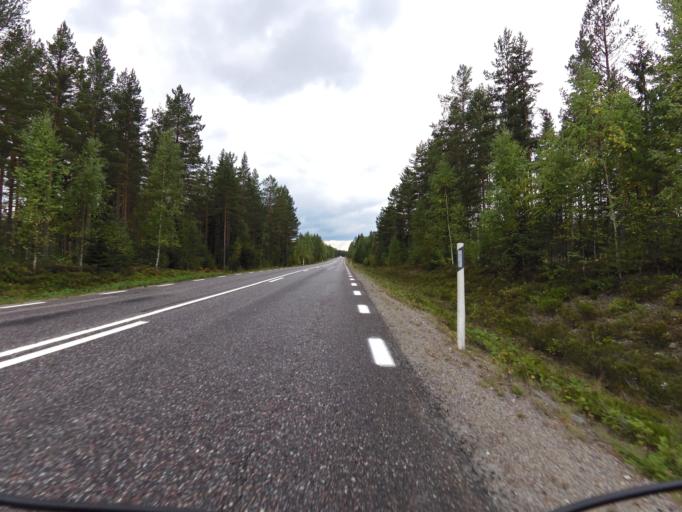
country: SE
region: Gaevleborg
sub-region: Ockelbo Kommun
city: Ockelbo
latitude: 60.8843
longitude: 16.9017
